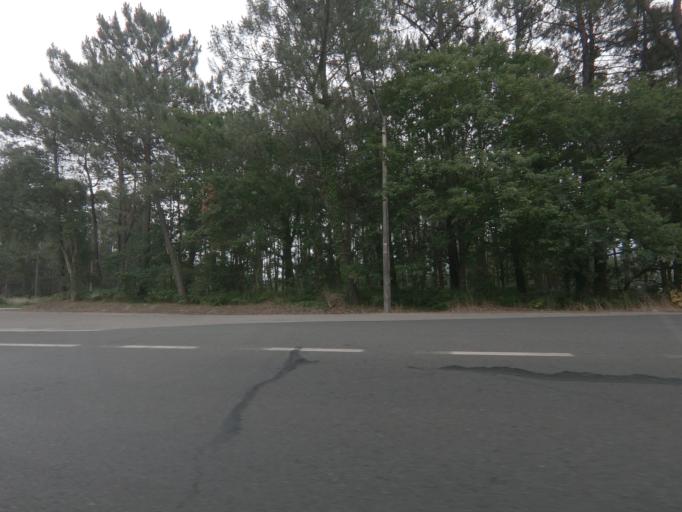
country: ES
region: Galicia
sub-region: Provincia de Pontevedra
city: Tomino
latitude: 41.9757
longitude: -8.7392
